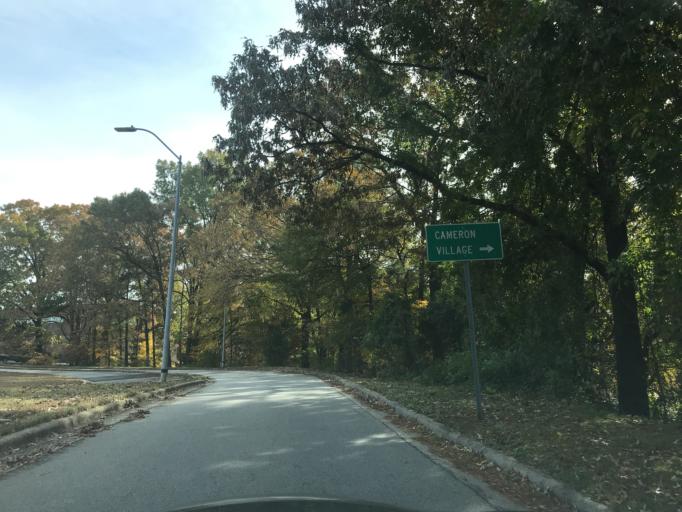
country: US
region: North Carolina
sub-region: Wake County
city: West Raleigh
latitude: 35.8001
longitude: -78.6618
